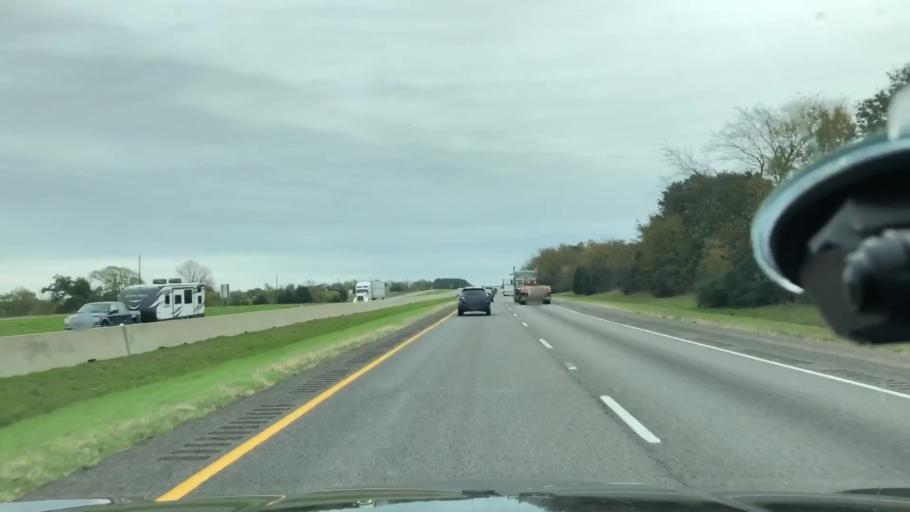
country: US
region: Texas
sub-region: Franklin County
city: Mount Vernon
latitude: 33.1672
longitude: -95.3458
